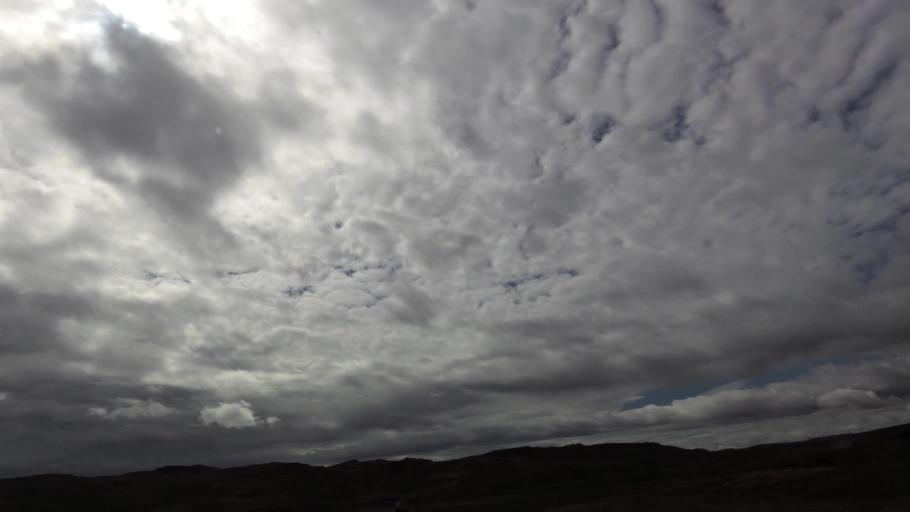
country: IS
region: West
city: Stykkisholmur
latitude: 65.5345
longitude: -22.0863
